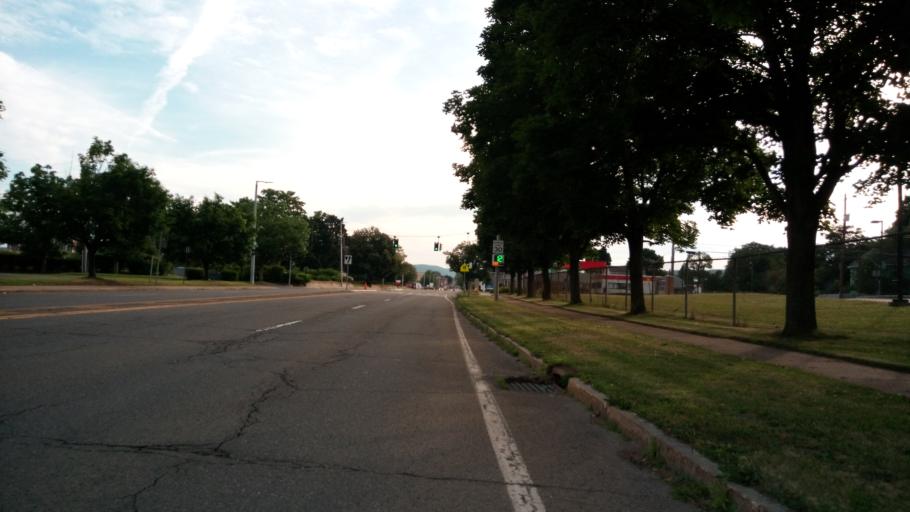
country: US
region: New York
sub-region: Chemung County
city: Elmira
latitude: 42.0944
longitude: -76.7931
